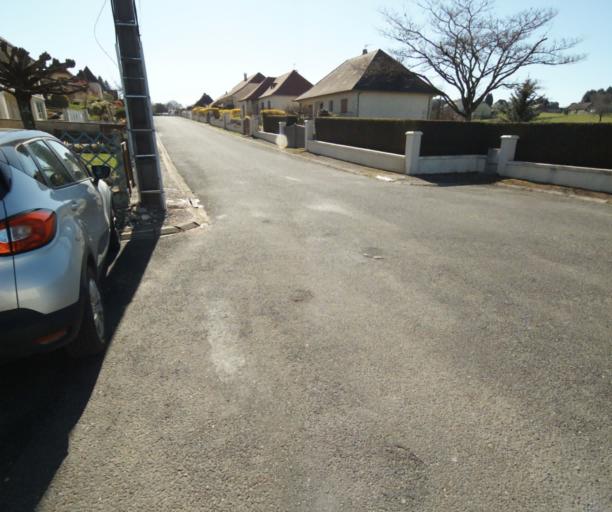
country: FR
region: Limousin
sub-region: Departement de la Correze
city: Seilhac
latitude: 45.3707
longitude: 1.7166
